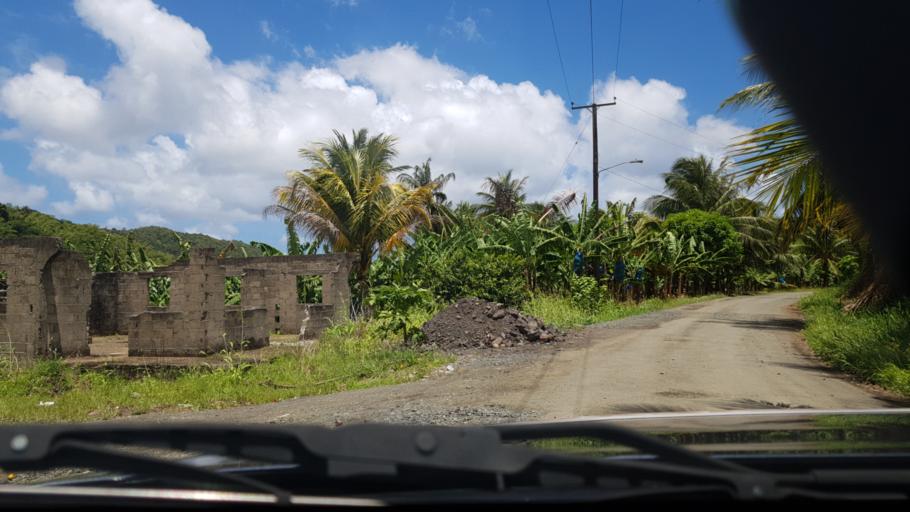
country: LC
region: Anse-la-Raye
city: Anse La Raye
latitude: 13.9477
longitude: -60.9912
